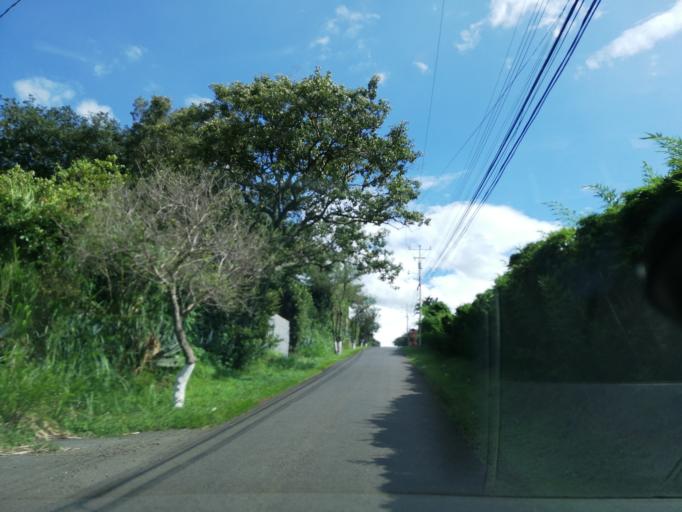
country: CR
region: Alajuela
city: Alajuela
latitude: 9.9831
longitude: -84.2188
